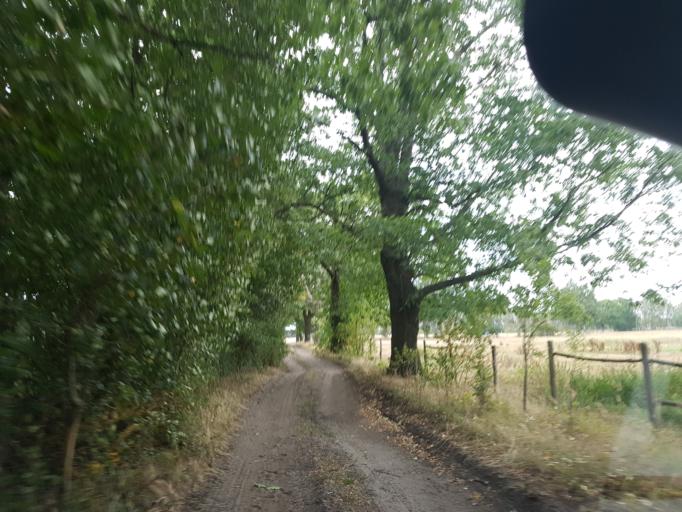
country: DE
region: Brandenburg
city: Schilda
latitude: 51.5706
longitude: 13.3464
